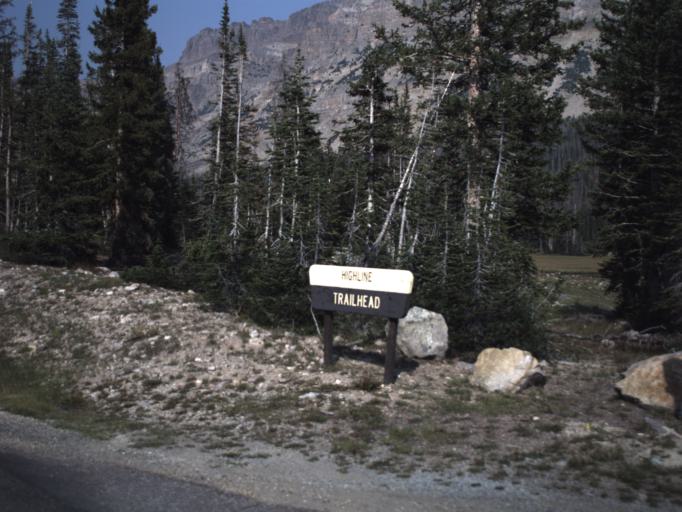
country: US
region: Utah
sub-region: Summit County
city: Kamas
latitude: 40.7237
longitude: -110.8650
